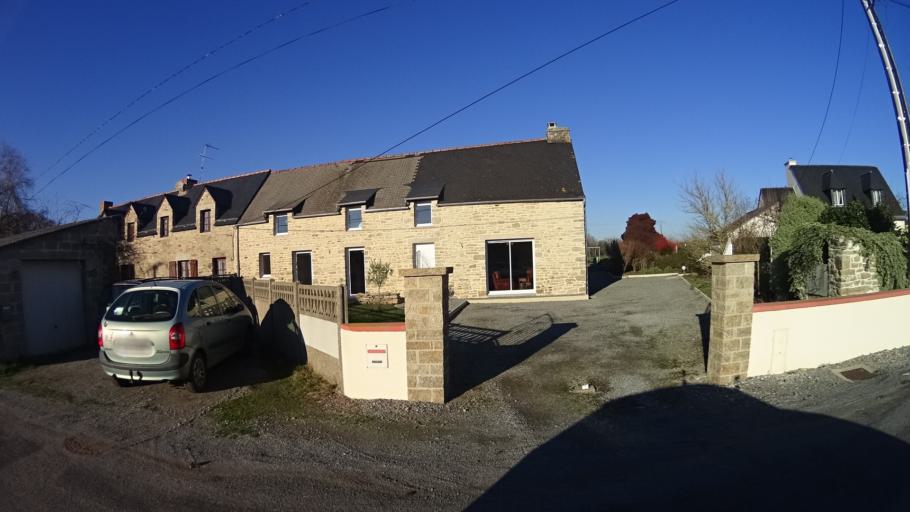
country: FR
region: Brittany
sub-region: Departement du Morbihan
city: Allaire
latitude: 47.6461
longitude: -2.1714
